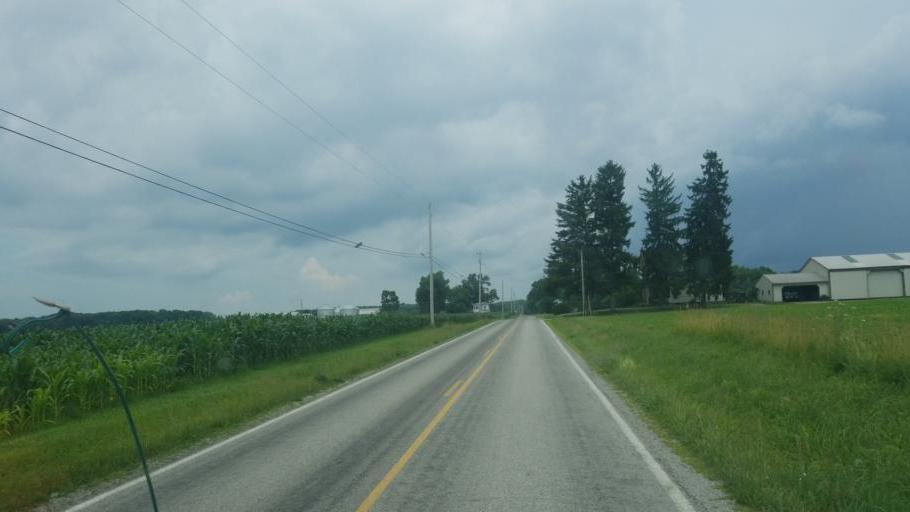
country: US
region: Ohio
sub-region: Wayne County
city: Wooster
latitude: 40.8919
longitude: -81.9535
